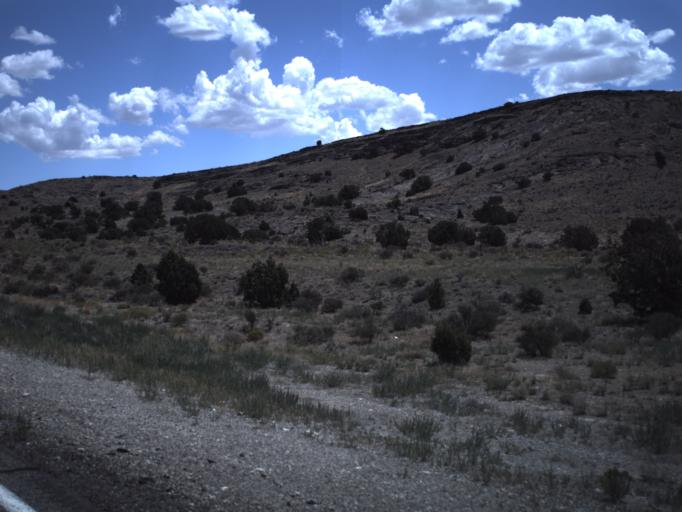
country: US
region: Utah
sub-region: Beaver County
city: Milford
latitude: 39.0791
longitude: -113.7027
